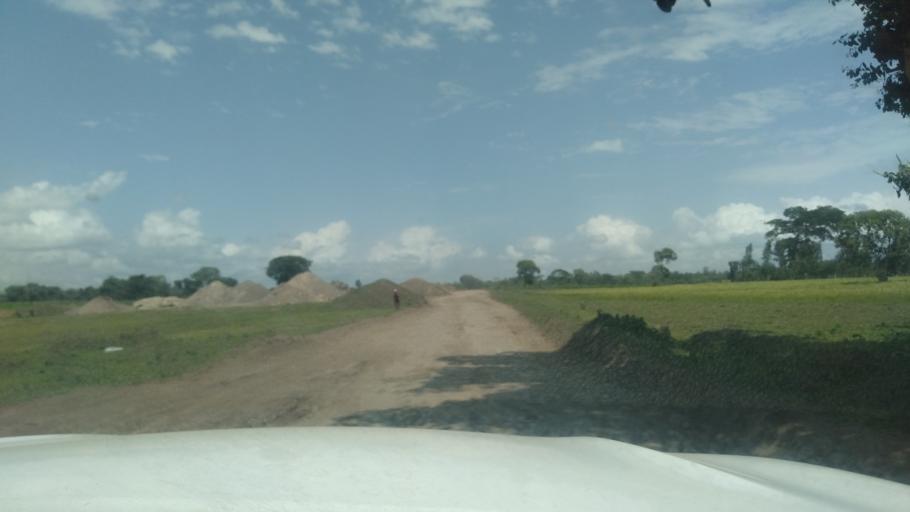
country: ET
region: Oromiya
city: Shashemene
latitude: 7.2739
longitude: 38.6009
